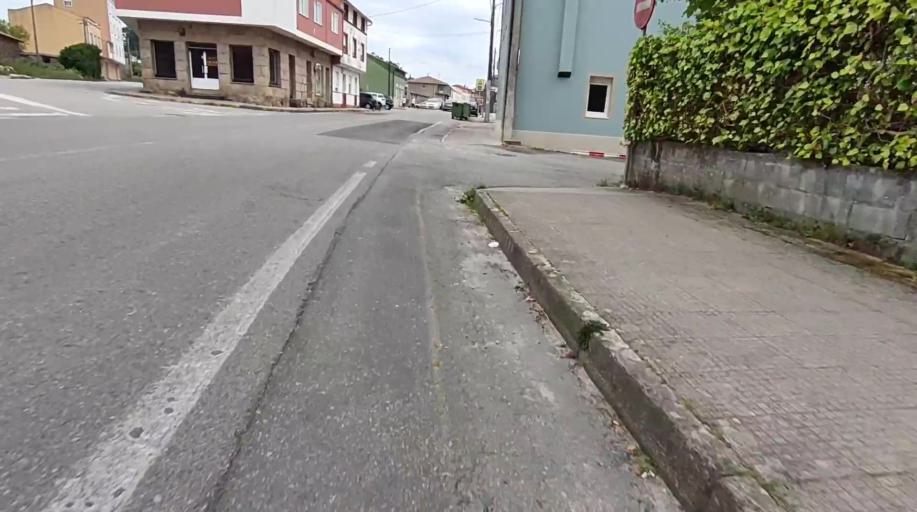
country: ES
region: Galicia
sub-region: Provincia da Coruna
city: Boiro
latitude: 42.6364
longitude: -8.8756
